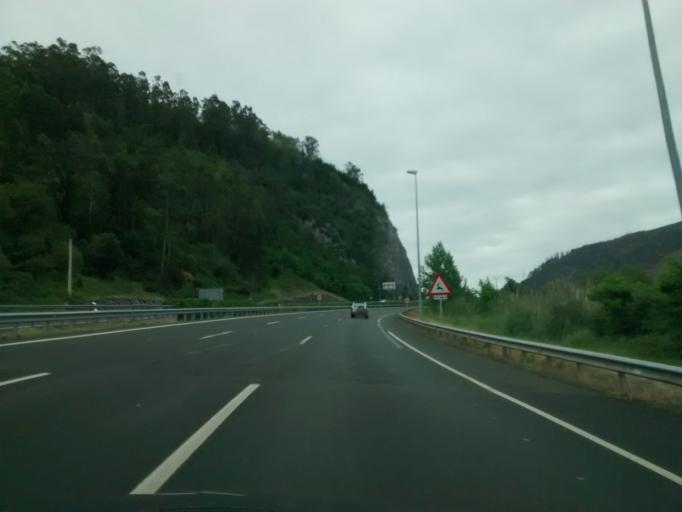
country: ES
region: Cantabria
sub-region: Provincia de Cantabria
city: Los Corrales de Buelna
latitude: 43.2870
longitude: -4.0808
